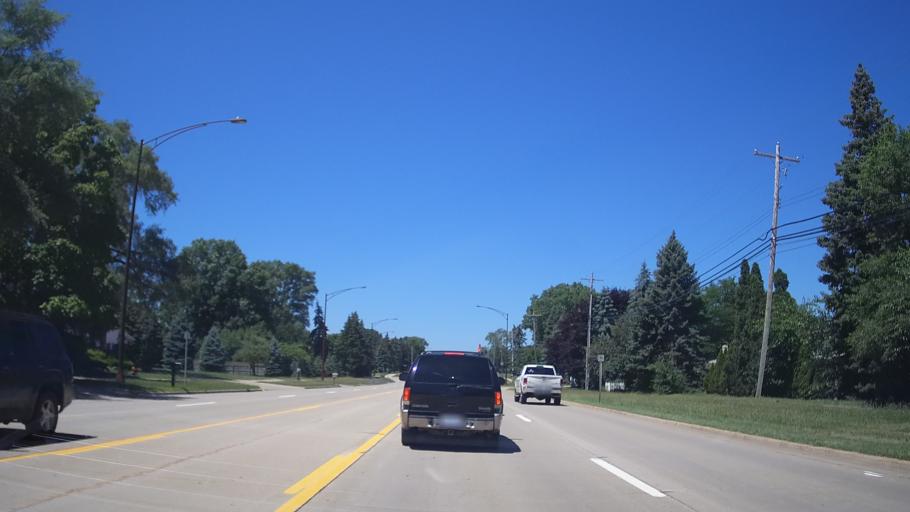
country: US
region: Michigan
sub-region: Oakland County
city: Troy
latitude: 42.5925
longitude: -83.1124
